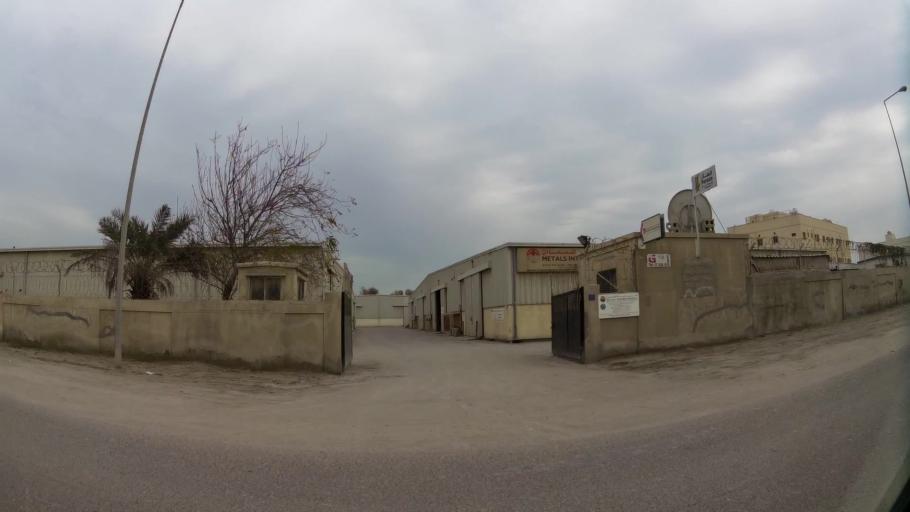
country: BH
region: Northern
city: Sitrah
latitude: 26.1745
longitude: 50.6099
